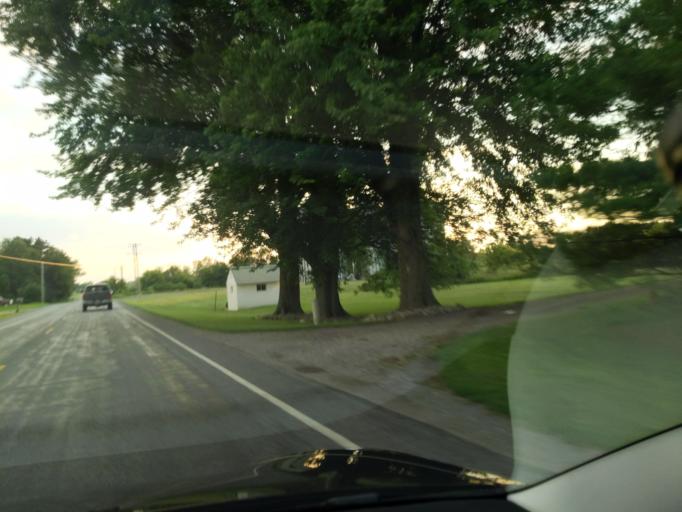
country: US
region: Michigan
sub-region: Ingham County
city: Mason
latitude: 42.5241
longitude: -84.4351
